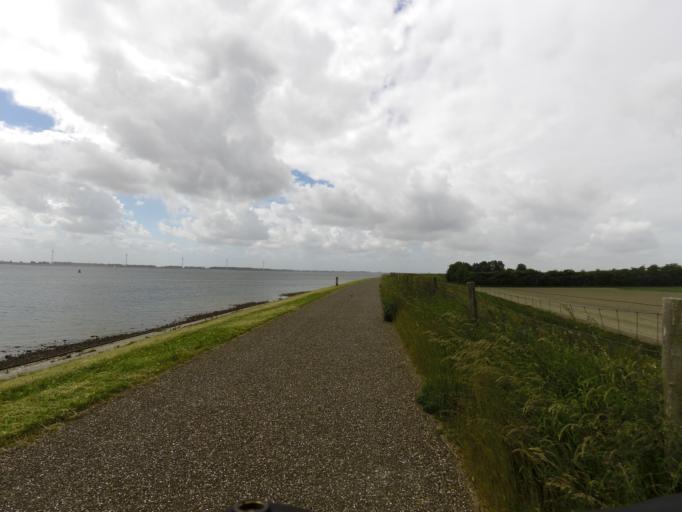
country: NL
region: Zeeland
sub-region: Schouwen-Duiveland
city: Bruinisse
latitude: 51.6330
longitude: 4.0715
